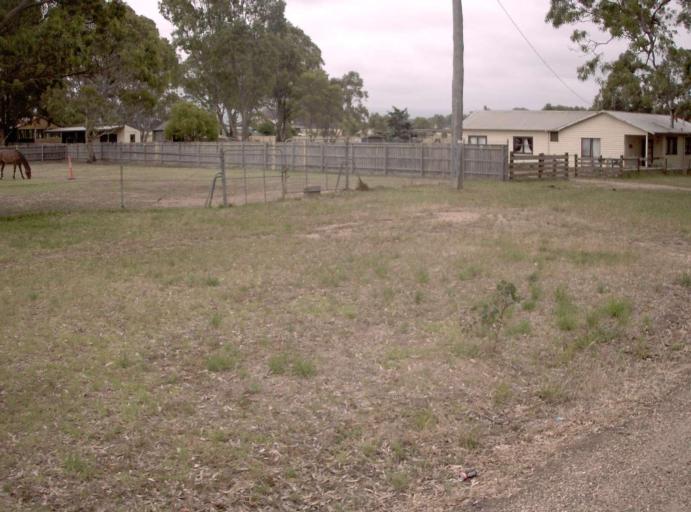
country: AU
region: Victoria
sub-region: Wellington
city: Heyfield
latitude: -37.9749
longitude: 146.7822
